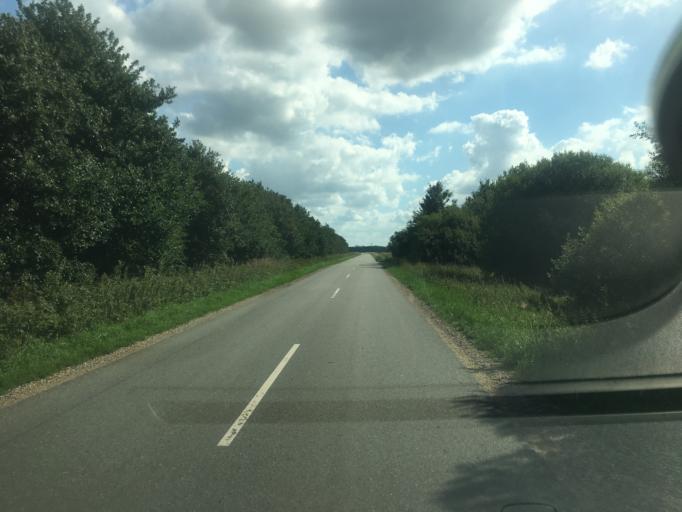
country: DE
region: Schleswig-Holstein
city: Ellhoft
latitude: 54.9598
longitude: 8.9608
